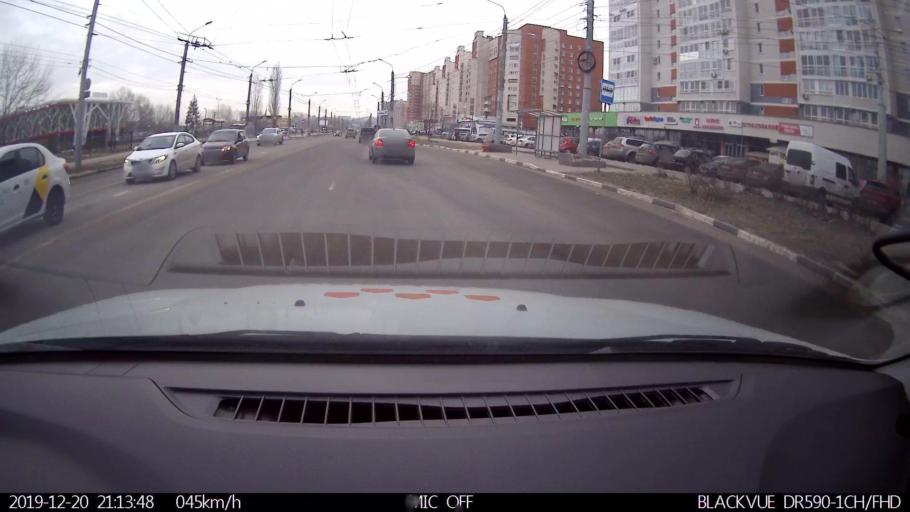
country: RU
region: Nizjnij Novgorod
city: Nizhniy Novgorod
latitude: 56.3407
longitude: 43.9298
